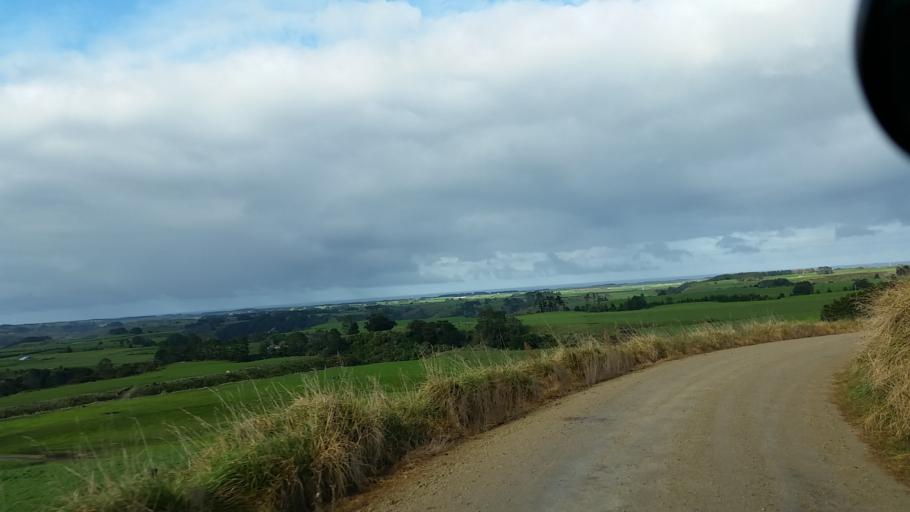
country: NZ
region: Taranaki
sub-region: South Taranaki District
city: Patea
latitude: -39.7293
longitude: 174.7103
